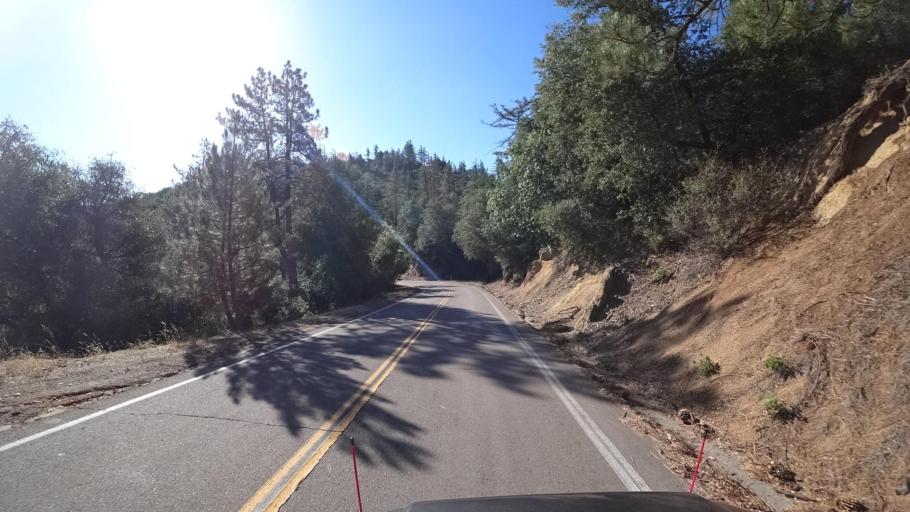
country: US
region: California
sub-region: Riverside County
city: Aguanga
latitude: 33.2870
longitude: -116.8021
